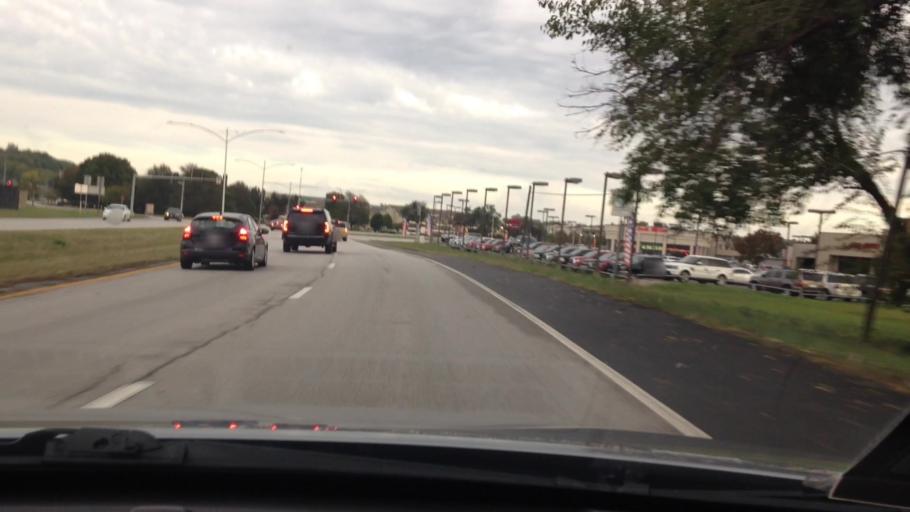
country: US
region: Missouri
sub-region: Clay County
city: North Kansas City
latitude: 39.1525
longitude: -94.5834
